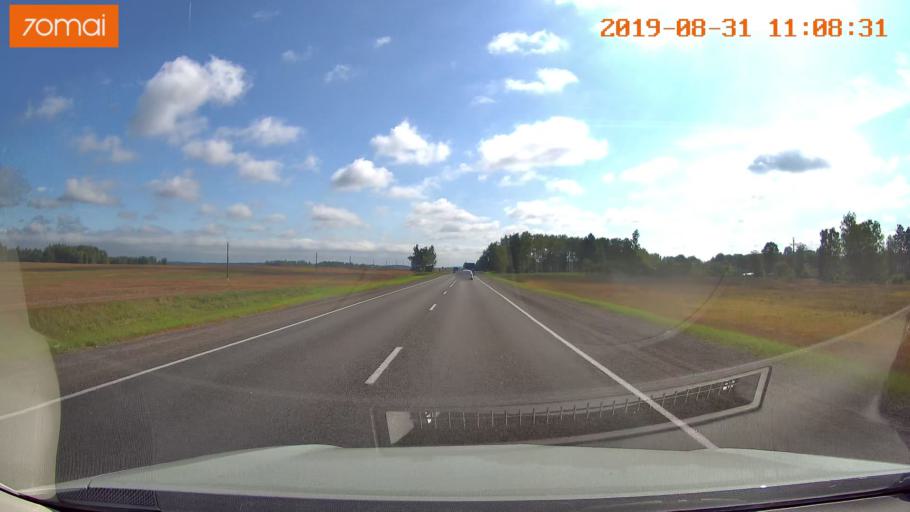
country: BY
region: Mogilev
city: Ramanavichy
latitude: 53.8272
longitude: 30.6885
